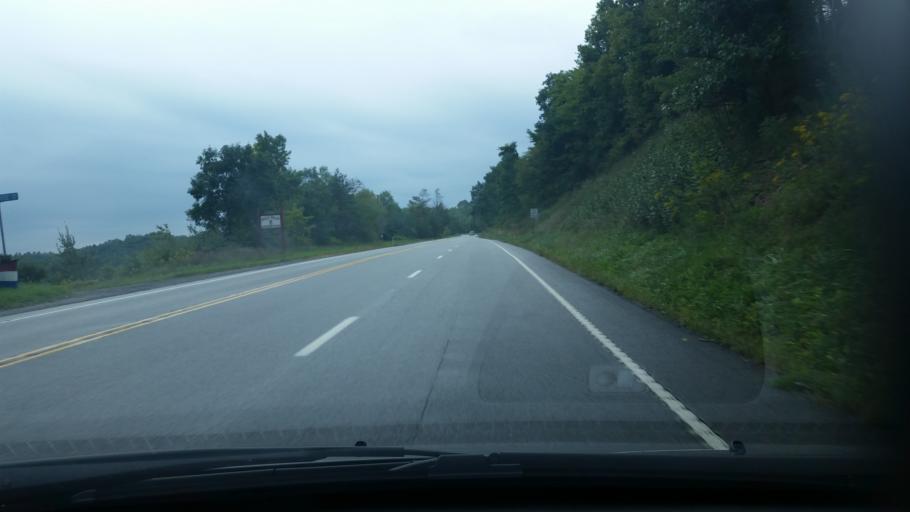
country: US
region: Pennsylvania
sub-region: Clearfield County
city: Shiloh
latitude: 41.0824
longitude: -78.2749
